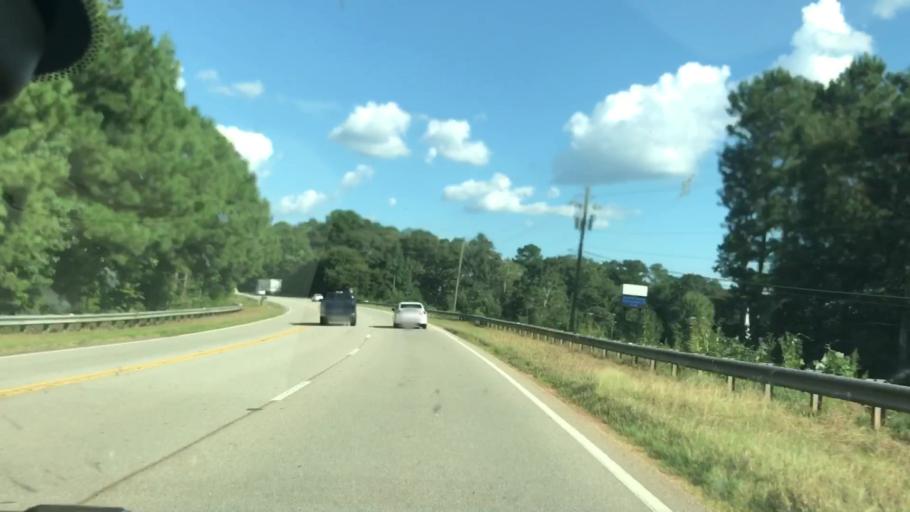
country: US
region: Georgia
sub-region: Troup County
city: La Grange
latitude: 32.9633
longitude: -84.9821
